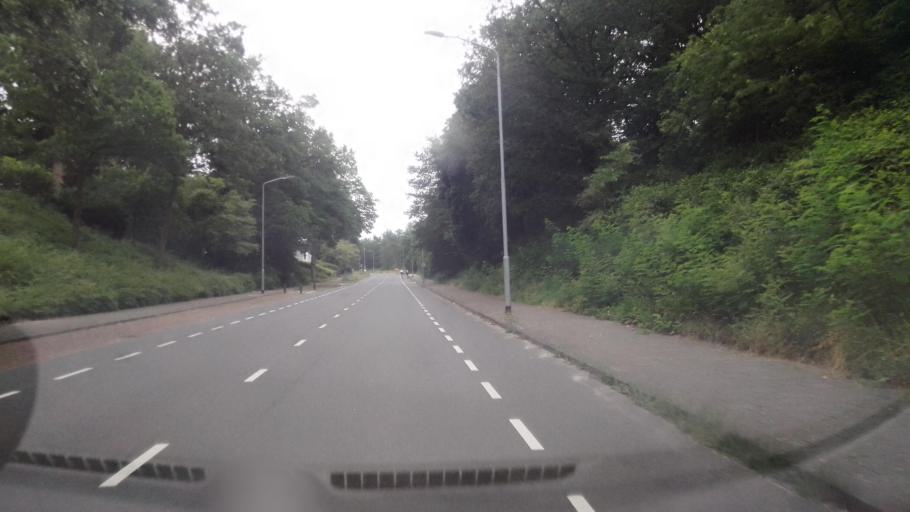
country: NL
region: Limburg
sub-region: Gemeente Venlo
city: Venlo
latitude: 51.3661
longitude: 6.1934
